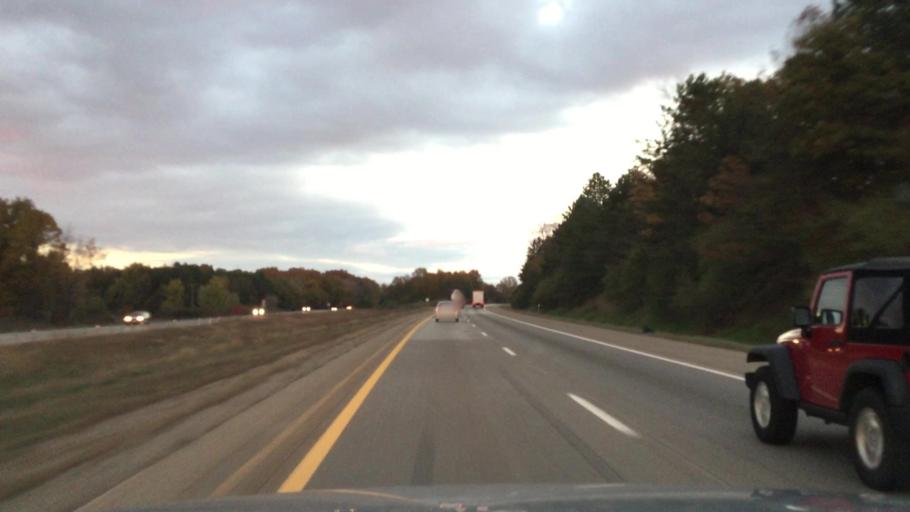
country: US
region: Michigan
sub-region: Jackson County
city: Grass Lake
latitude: 42.2880
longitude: -84.2756
